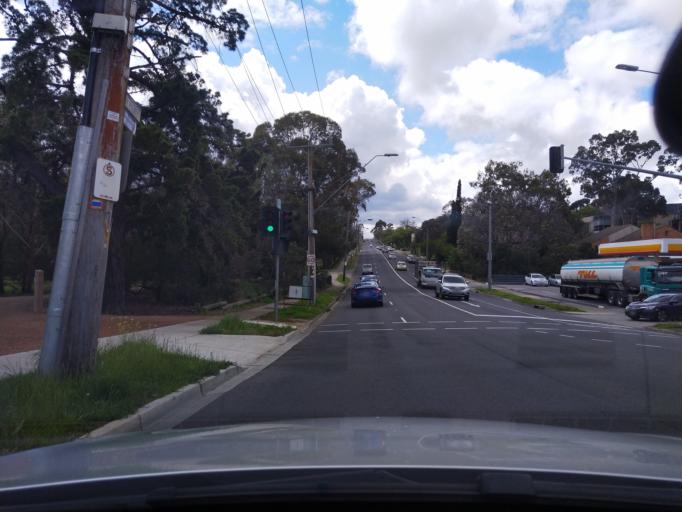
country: AU
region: Victoria
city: Rosanna
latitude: -37.7422
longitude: 145.0662
